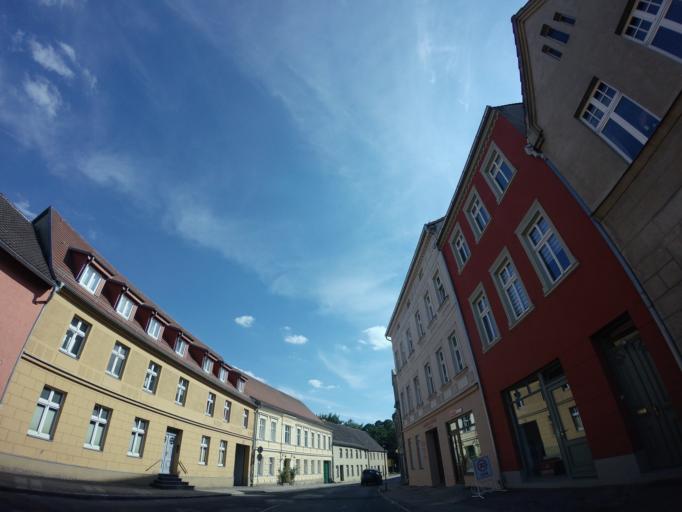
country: DE
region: Brandenburg
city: Rheinsberg
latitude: 53.0980
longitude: 12.8923
